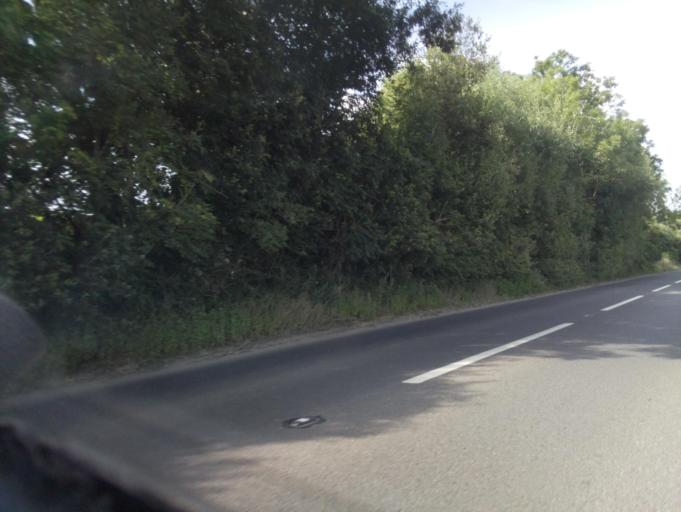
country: GB
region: England
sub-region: Wiltshire
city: Leigh
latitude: 51.6628
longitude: -1.9116
